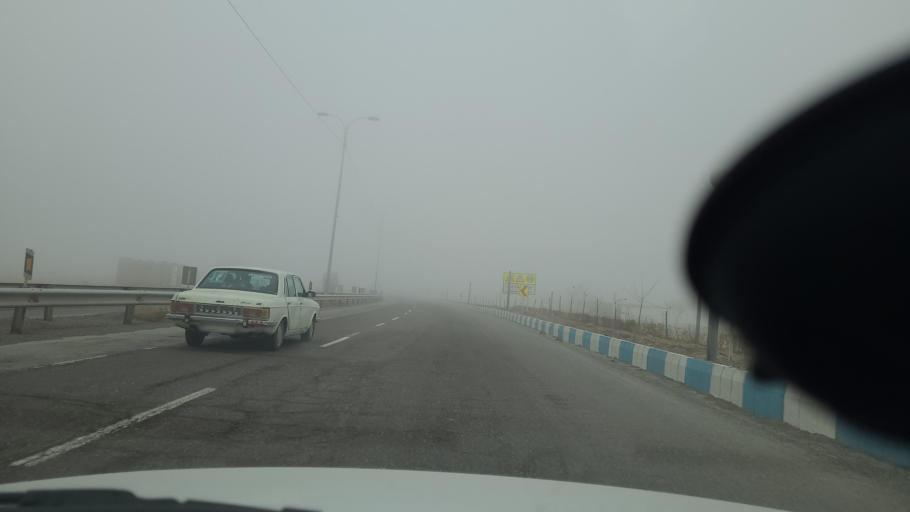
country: IR
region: Razavi Khorasan
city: Fariman
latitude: 35.7780
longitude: 59.7387
